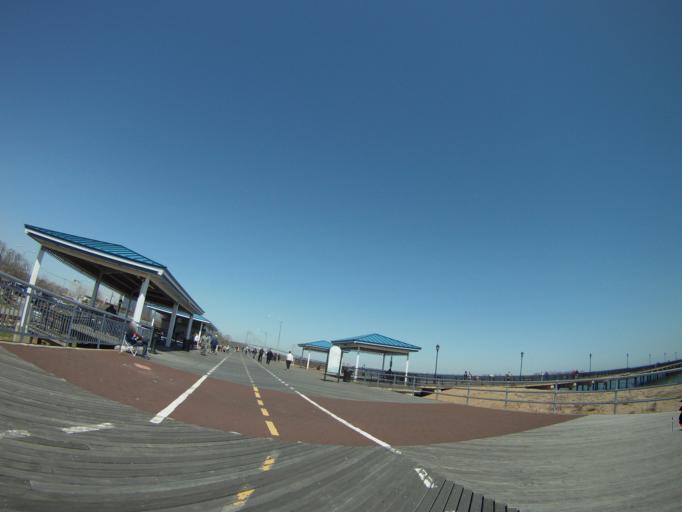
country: US
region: New York
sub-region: Richmond County
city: Staten Island
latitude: 40.5794
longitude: -74.0761
